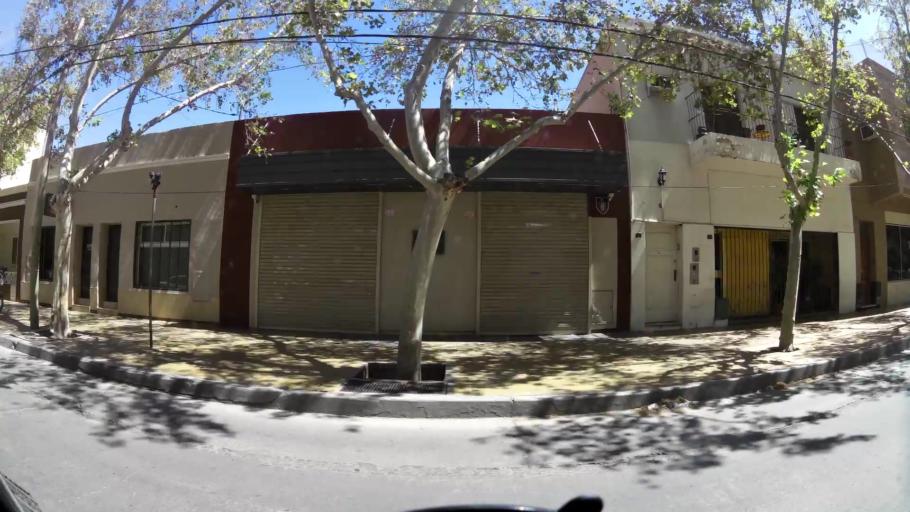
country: AR
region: San Juan
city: San Juan
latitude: -31.5354
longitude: -68.5205
